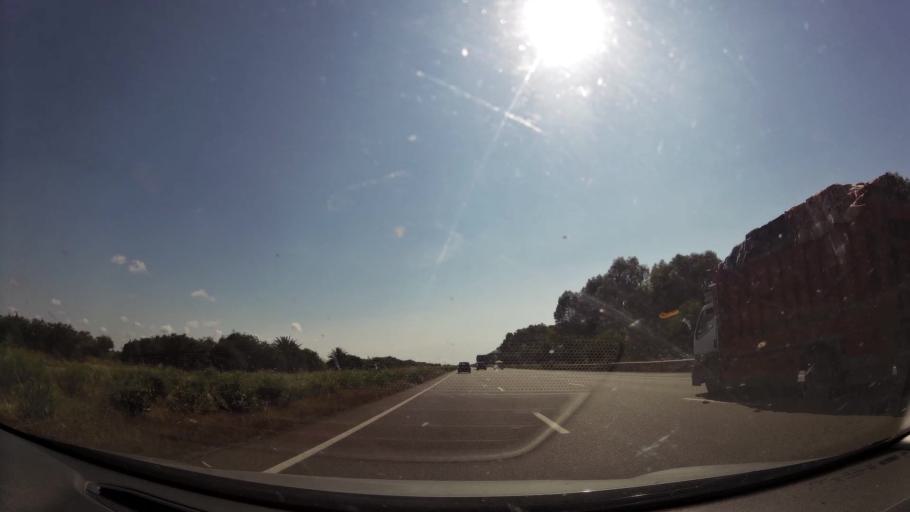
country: MA
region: Chaouia-Ouardigha
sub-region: Benslimane
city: Bouznika
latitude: 33.7942
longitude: -7.1901
